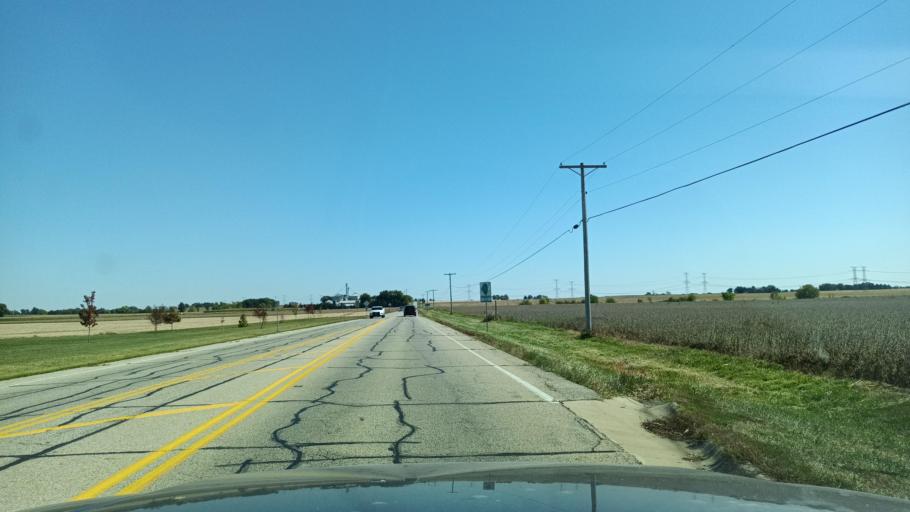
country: US
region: Illinois
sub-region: Tazewell County
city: Morton
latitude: 40.6134
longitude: -89.4306
